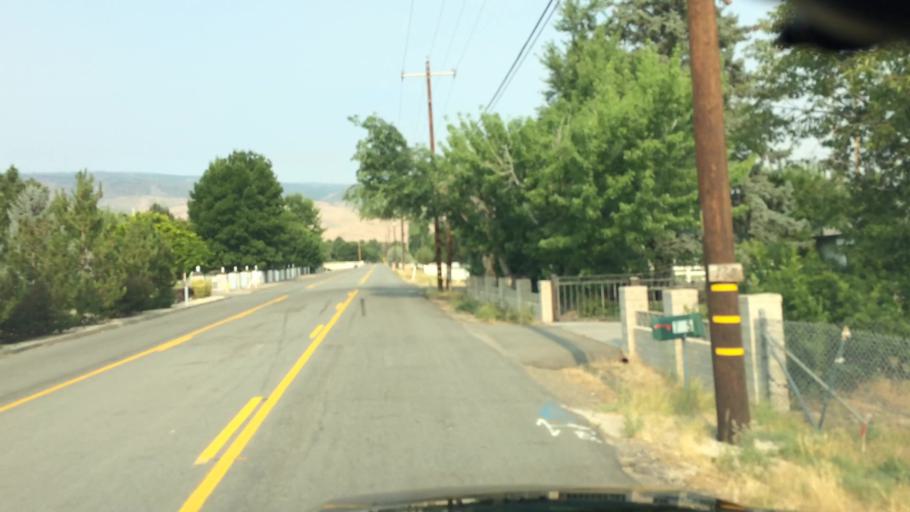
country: US
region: Nevada
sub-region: Washoe County
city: Reno
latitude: 39.4439
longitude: -119.7816
